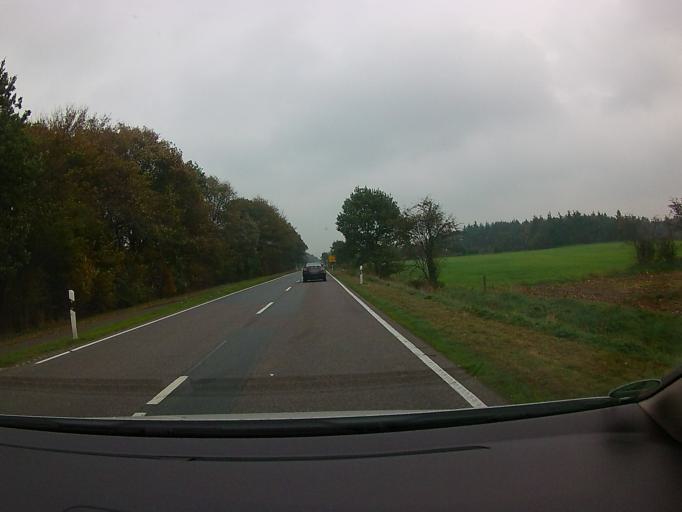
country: DE
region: Schleswig-Holstein
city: Goldebek
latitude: 54.6761
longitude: 9.1390
